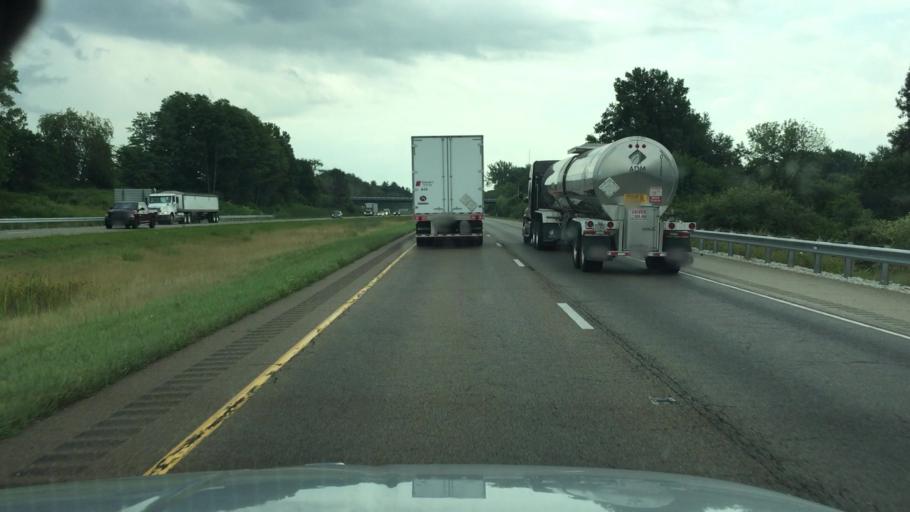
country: US
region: Illinois
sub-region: Peoria County
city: Bellevue
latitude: 40.7655
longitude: -89.7315
